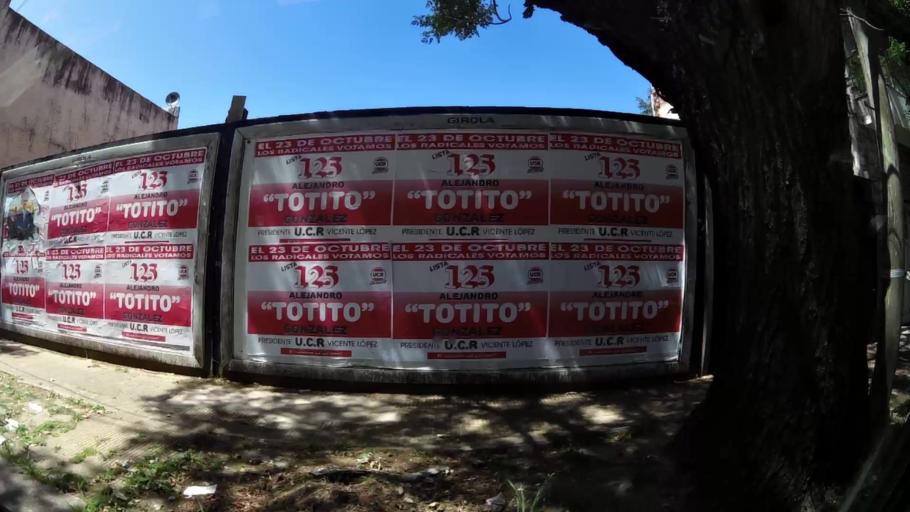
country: AR
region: Buenos Aires
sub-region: Partido de Vicente Lopez
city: Olivos
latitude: -34.5121
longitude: -58.5007
